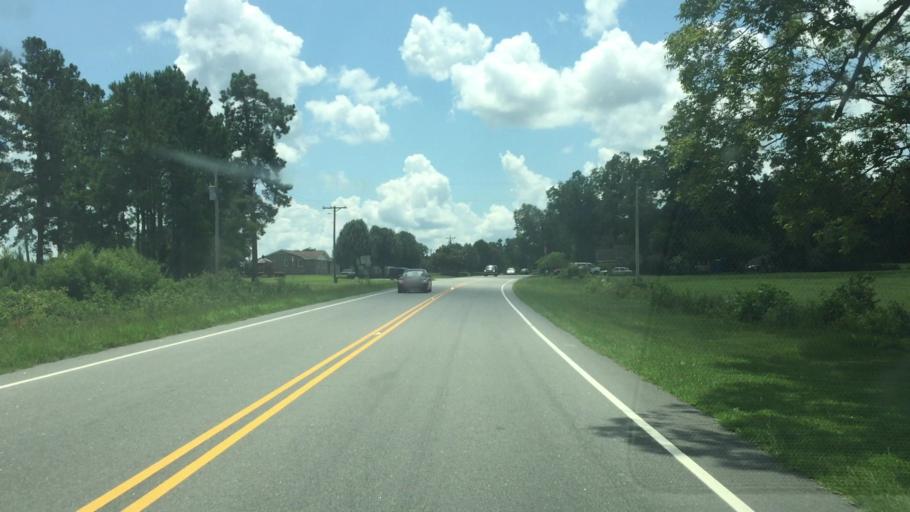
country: US
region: North Carolina
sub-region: Columbus County
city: Chadbourn
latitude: 34.2484
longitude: -78.8194
